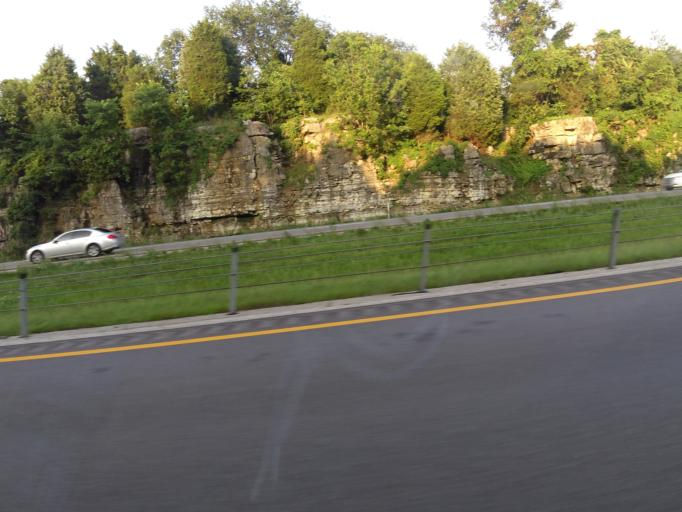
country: US
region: Kentucky
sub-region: Rockcastle County
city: Mount Vernon
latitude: 37.4090
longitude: -84.3402
